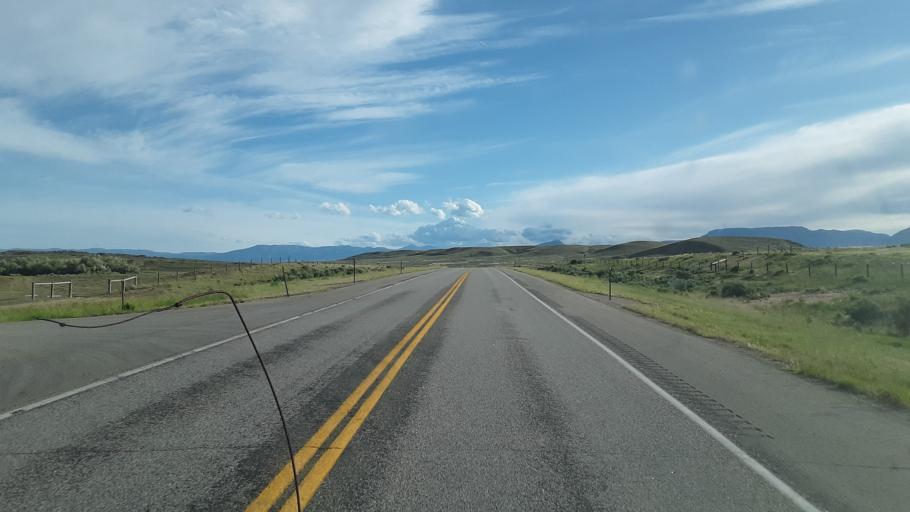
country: US
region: Montana
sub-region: Carbon County
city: Red Lodge
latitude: 44.9577
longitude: -109.0650
